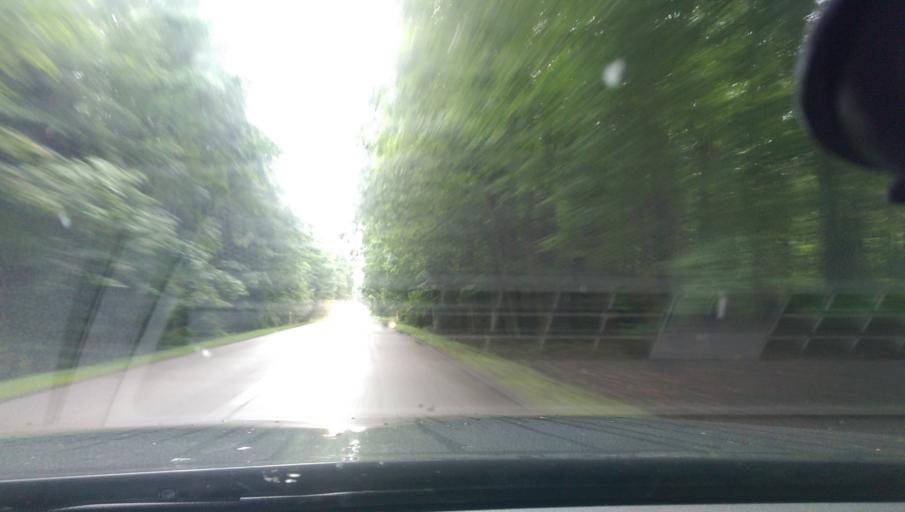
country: PL
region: Warmian-Masurian Voivodeship
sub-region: Powiat mragowski
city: Piecki
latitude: 53.7123
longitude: 21.4329
